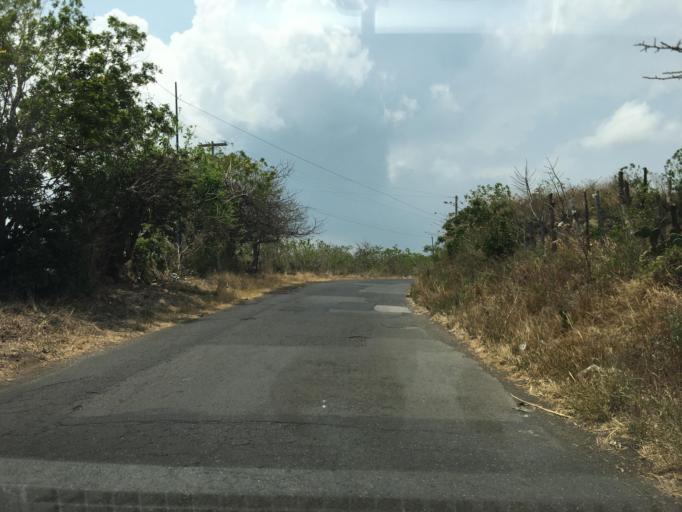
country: GT
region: Escuintla
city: San Vicente Pacaya
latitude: 14.3609
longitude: -90.5693
